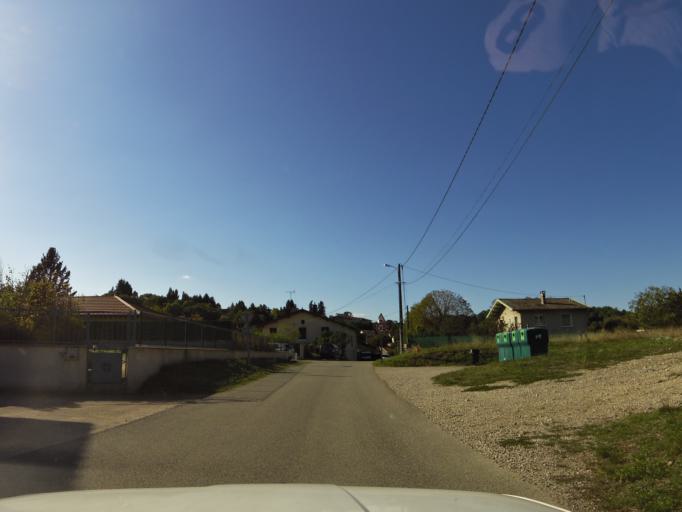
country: FR
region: Rhone-Alpes
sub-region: Departement de l'Ain
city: Meximieux
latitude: 45.9101
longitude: 5.2118
